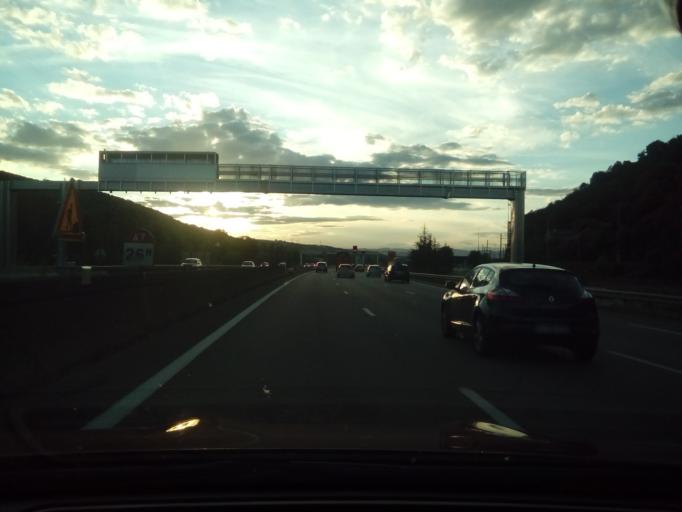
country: FR
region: Rhone-Alpes
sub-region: Departement de l'Isere
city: Seyssuel
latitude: 45.5449
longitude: 4.8403
